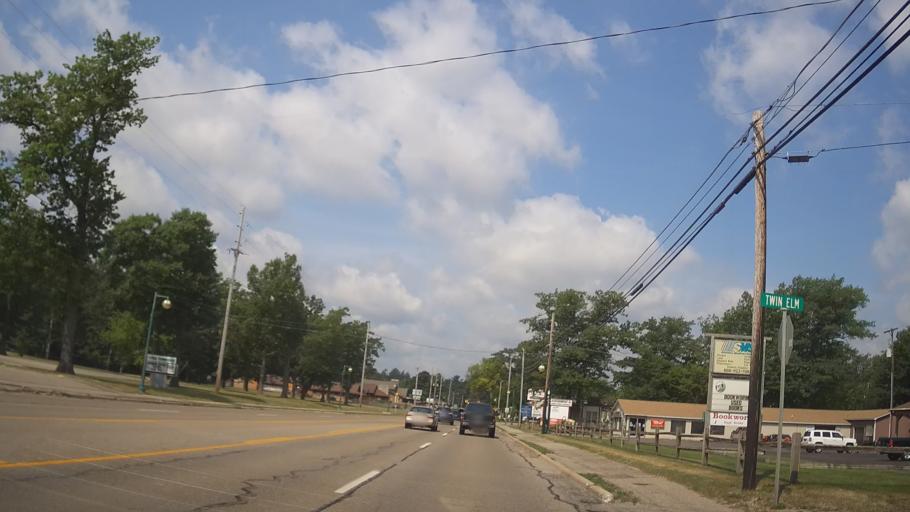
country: US
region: Michigan
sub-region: Roscommon County
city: Houghton Lake
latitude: 44.2983
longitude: -84.7283
